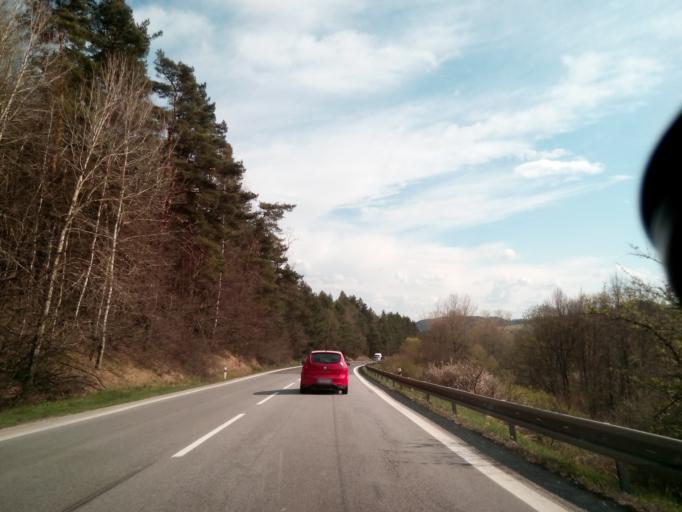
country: SK
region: Presovsky
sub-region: Okres Presov
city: Levoca
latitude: 49.0230
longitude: 20.6203
